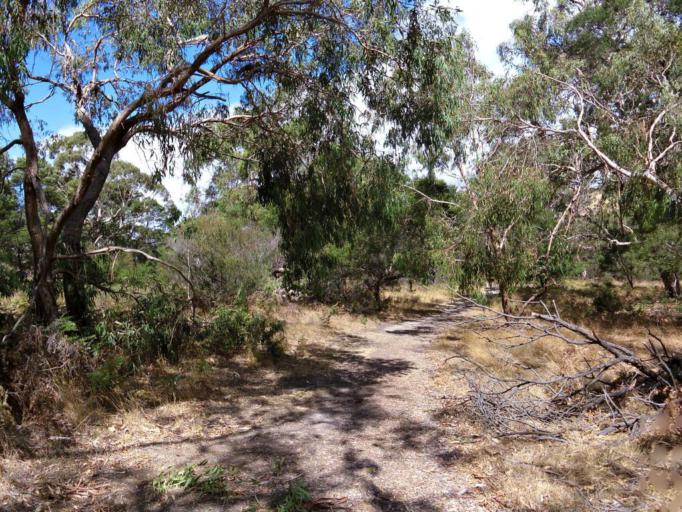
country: AU
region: Victoria
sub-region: Mornington Peninsula
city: Mount Martha
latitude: -38.2651
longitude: 145.0433
